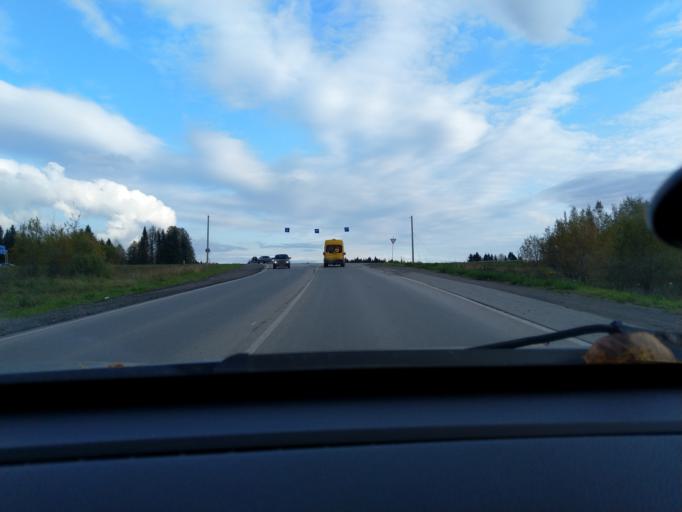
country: RU
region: Perm
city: Polazna
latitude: 58.2749
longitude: 56.4157
